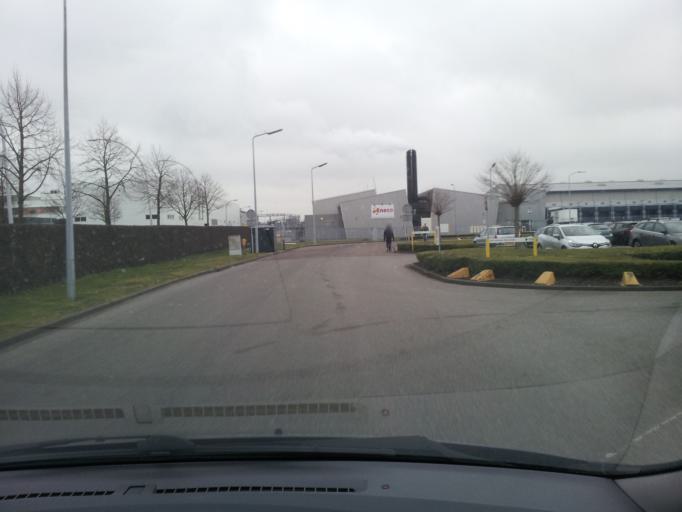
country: NL
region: South Holland
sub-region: Gemeente Den Haag
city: Ypenburg
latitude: 52.0440
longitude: 4.3584
